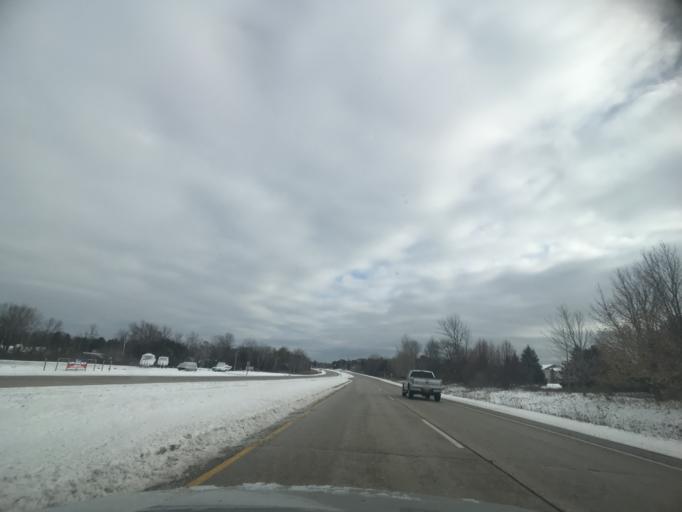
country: US
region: Wisconsin
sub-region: Door County
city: Sturgeon Bay
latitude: 44.8197
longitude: -87.3739
